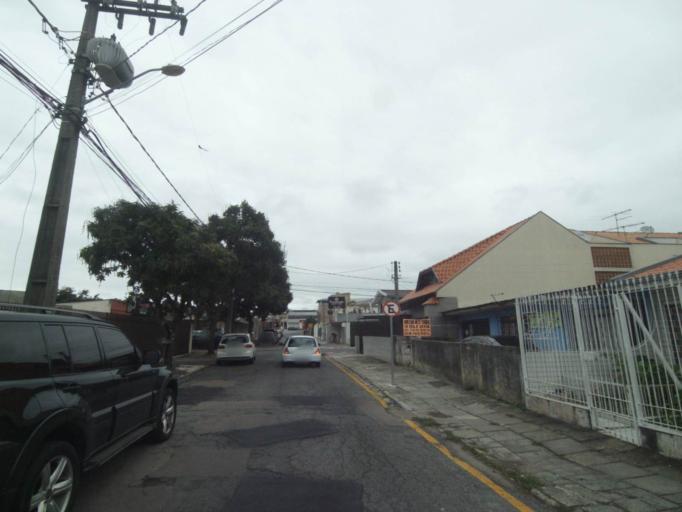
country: BR
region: Parana
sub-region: Curitiba
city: Curitiba
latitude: -25.4931
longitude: -49.2814
